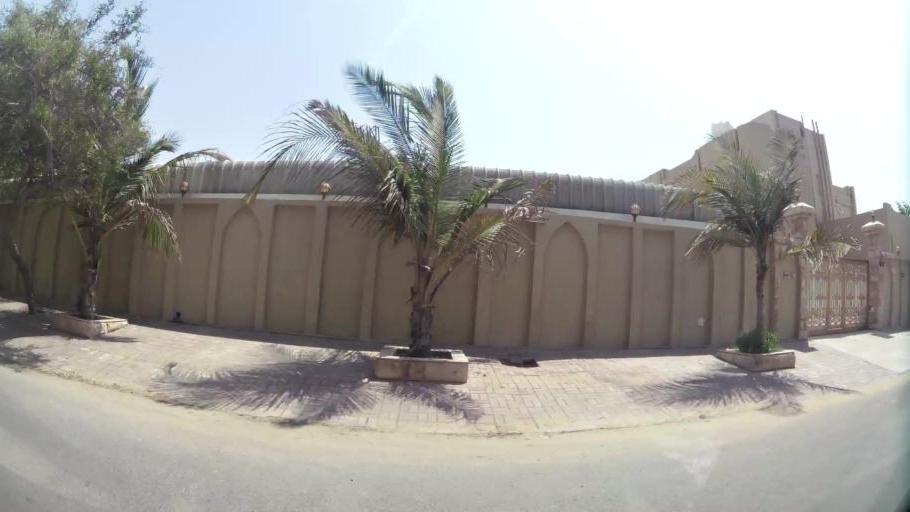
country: AE
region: Ajman
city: Ajman
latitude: 25.3981
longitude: 55.4277
